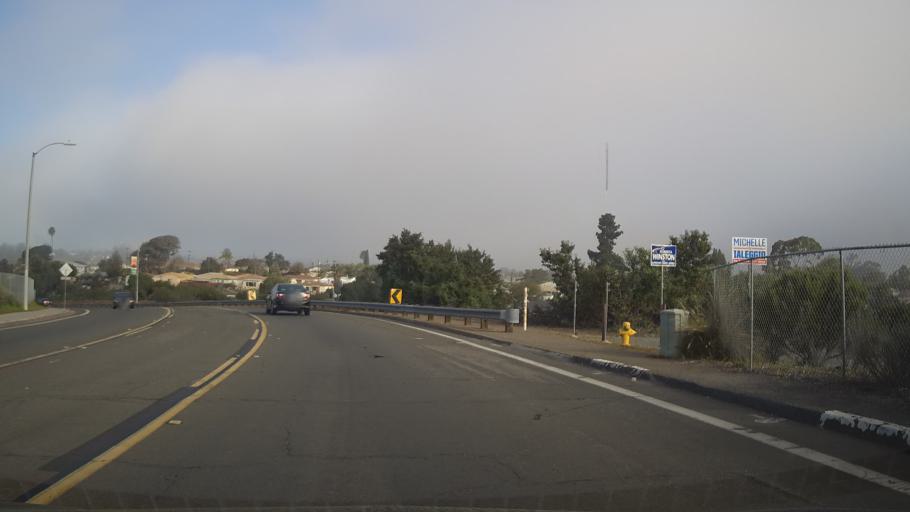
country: US
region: California
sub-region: San Diego County
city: National City
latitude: 32.7263
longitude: -117.0850
